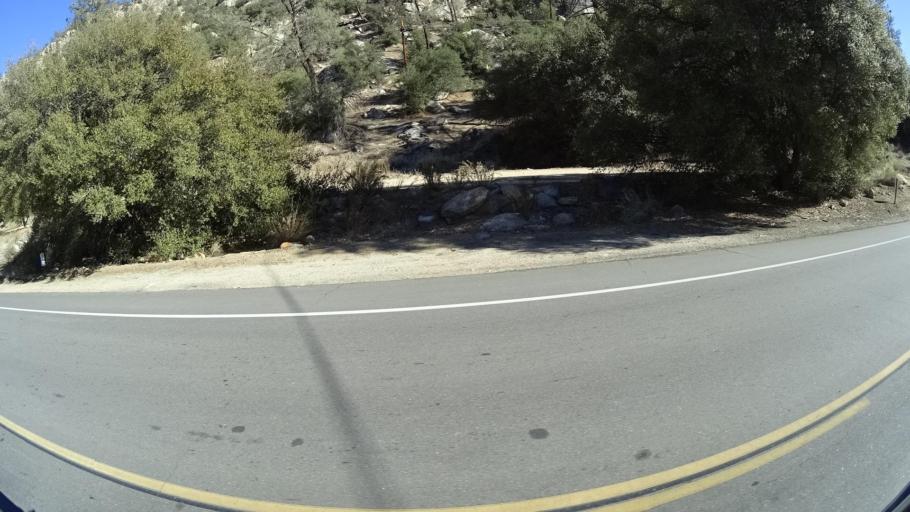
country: US
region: California
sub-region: Kern County
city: Kernville
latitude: 35.7460
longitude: -118.4140
